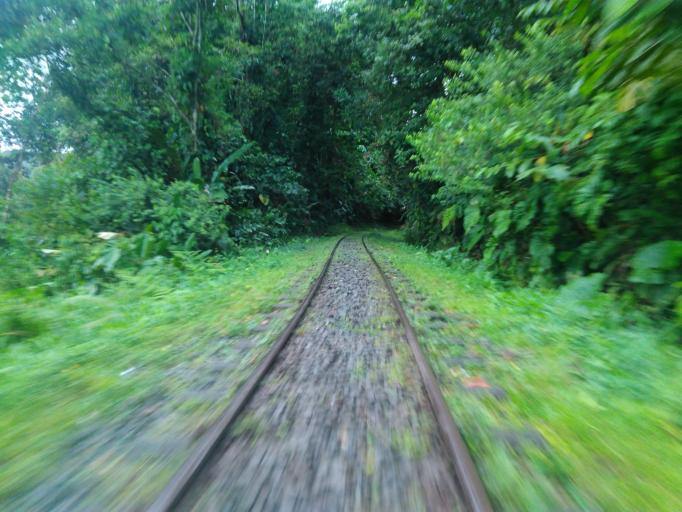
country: CO
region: Valle del Cauca
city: Buenaventura
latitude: 3.8412
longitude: -76.8744
